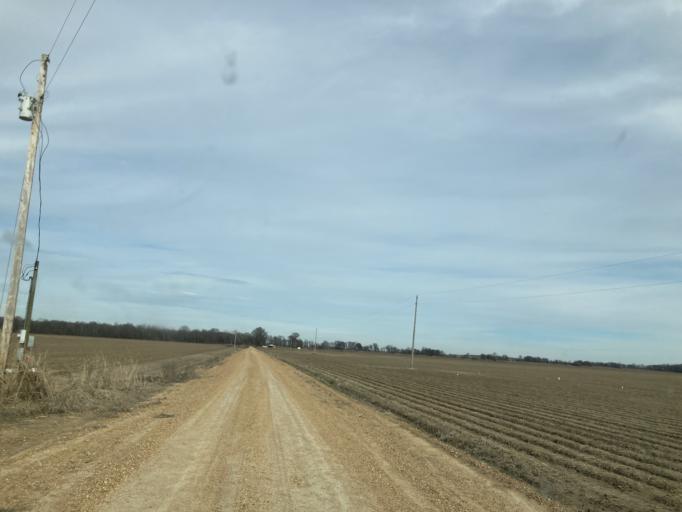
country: US
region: Mississippi
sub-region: Humphreys County
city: Belzoni
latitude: 33.0599
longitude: -90.6577
